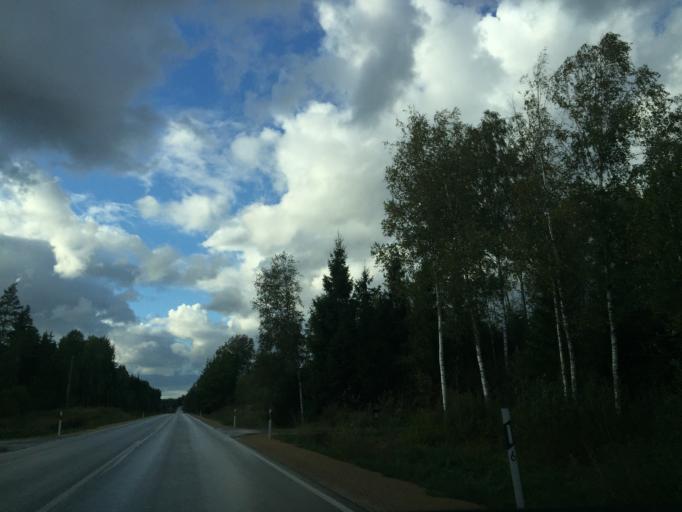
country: LV
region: Ligatne
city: Ligatne
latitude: 57.1556
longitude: 25.0666
